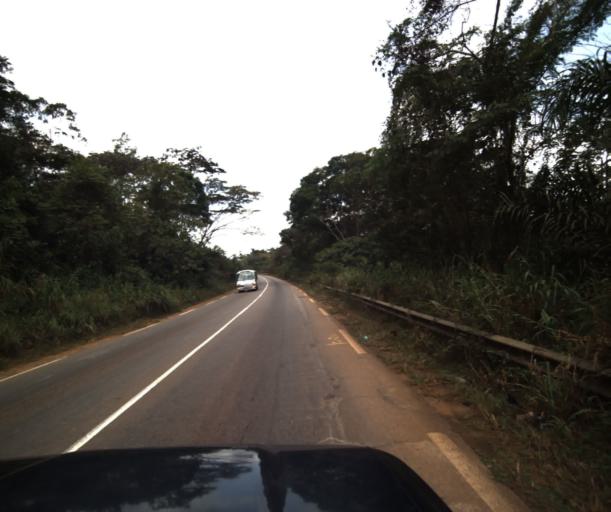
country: CM
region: Centre
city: Mbankomo
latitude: 3.7908
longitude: 11.3089
